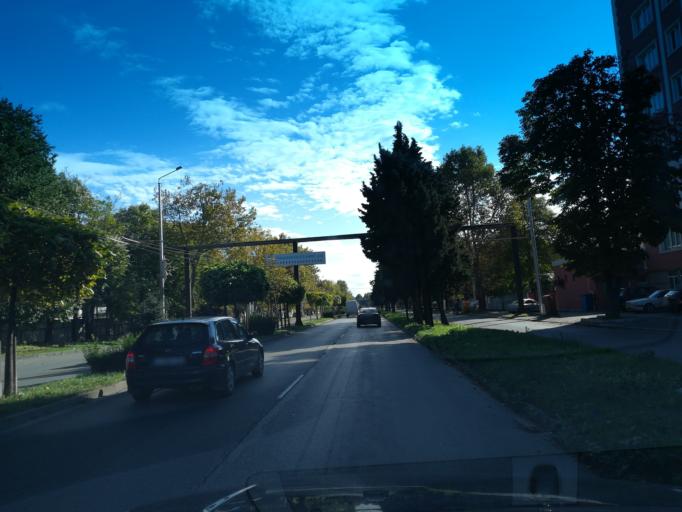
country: BG
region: Stara Zagora
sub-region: Obshtina Stara Zagora
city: Stara Zagora
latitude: 42.4126
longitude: 25.6389
